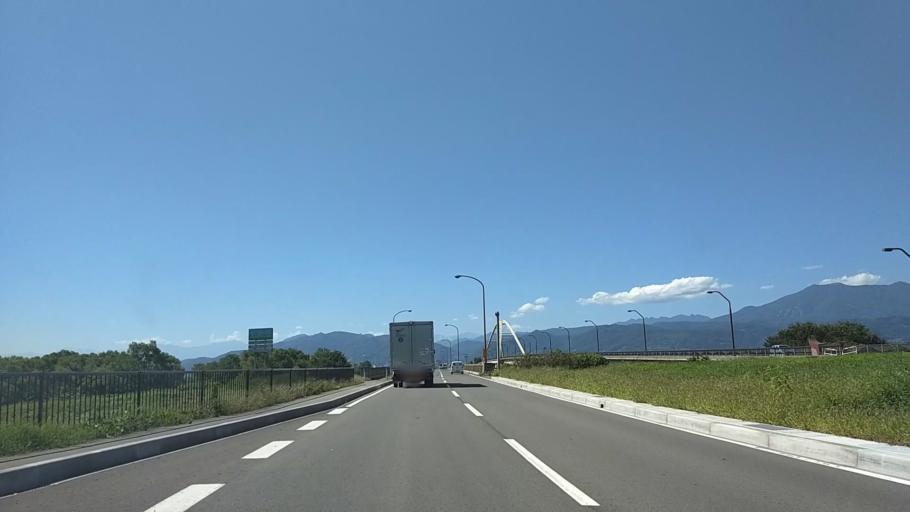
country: JP
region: Nagano
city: Suzaka
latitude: 36.6391
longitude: 138.2637
